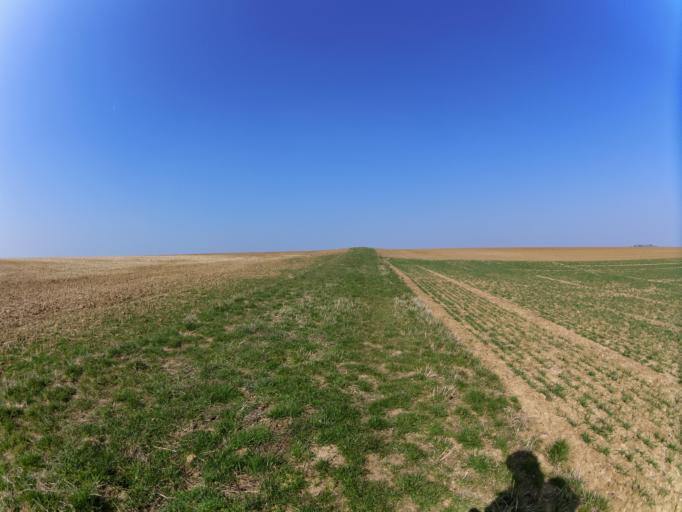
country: DE
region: Bavaria
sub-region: Regierungsbezirk Unterfranken
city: Winterhausen
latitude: 49.6874
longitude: 9.9804
